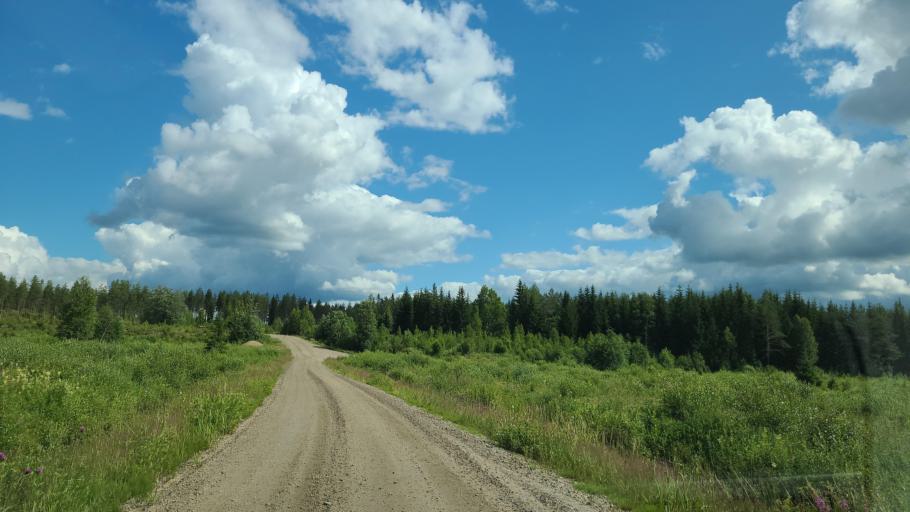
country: FI
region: Northern Savo
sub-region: Koillis-Savo
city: Kaavi
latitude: 63.0275
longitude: 28.7813
